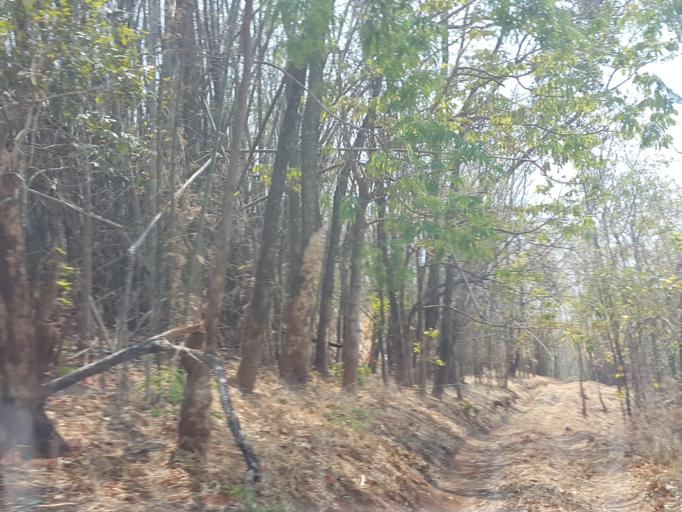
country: TH
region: Chiang Mai
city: Samoeng
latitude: 18.7925
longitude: 98.8224
